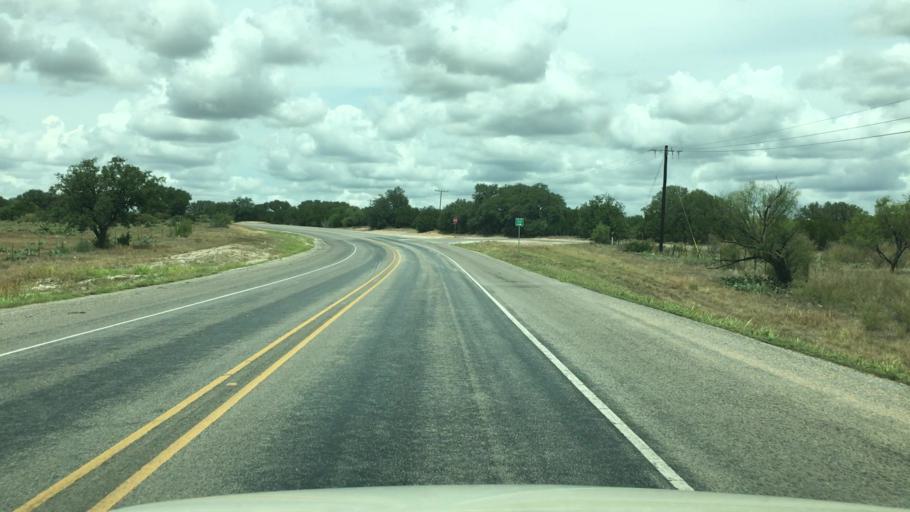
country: US
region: Texas
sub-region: McCulloch County
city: Brady
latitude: 31.0167
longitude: -99.2108
